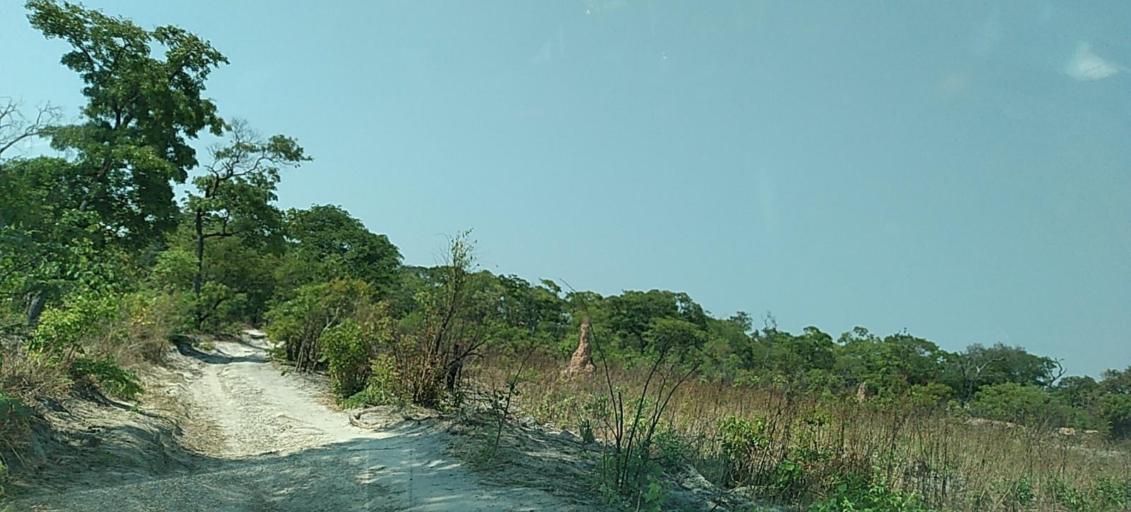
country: ZM
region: Copperbelt
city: Mpongwe
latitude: -13.7778
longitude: 28.1073
